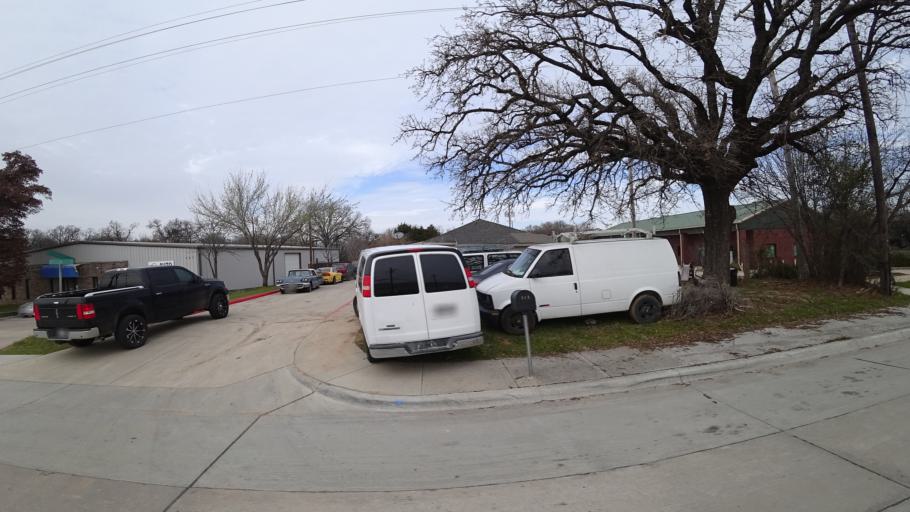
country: US
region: Texas
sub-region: Denton County
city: Lewisville
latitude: 33.0274
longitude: -96.9840
